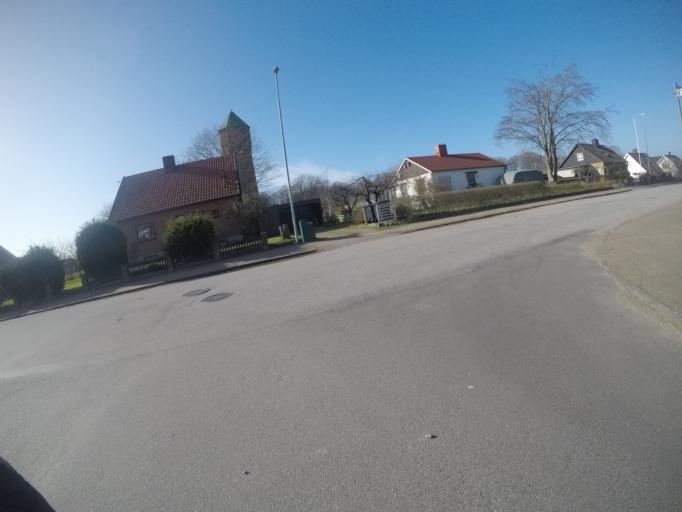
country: SE
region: Halland
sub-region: Laholms Kommun
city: Laholm
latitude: 56.5056
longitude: 13.0454
